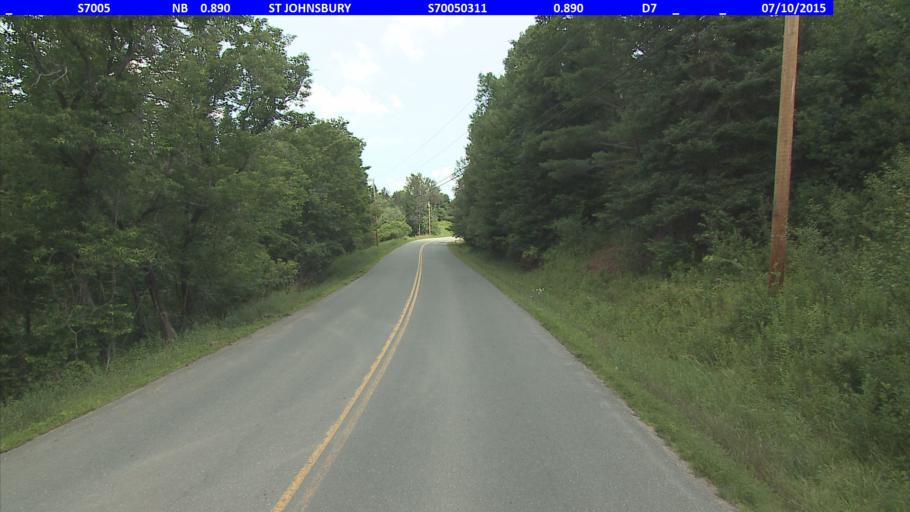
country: US
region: Vermont
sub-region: Caledonia County
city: St Johnsbury
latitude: 44.4464
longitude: -72.0061
